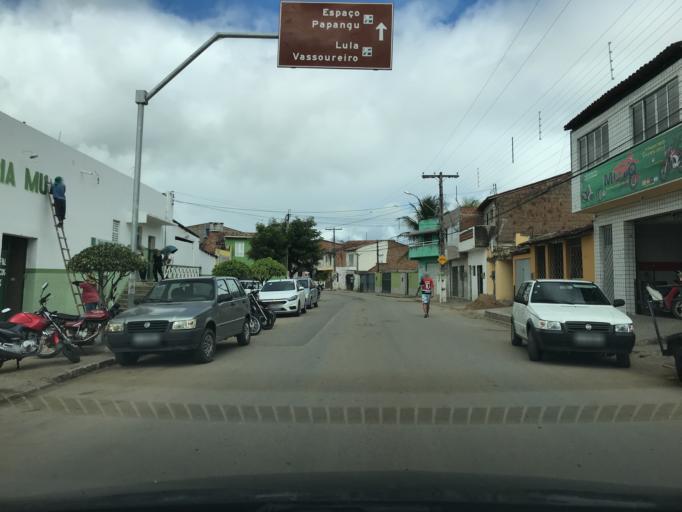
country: BR
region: Pernambuco
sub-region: Bezerros
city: Bezerros
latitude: -8.2295
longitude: -35.7513
